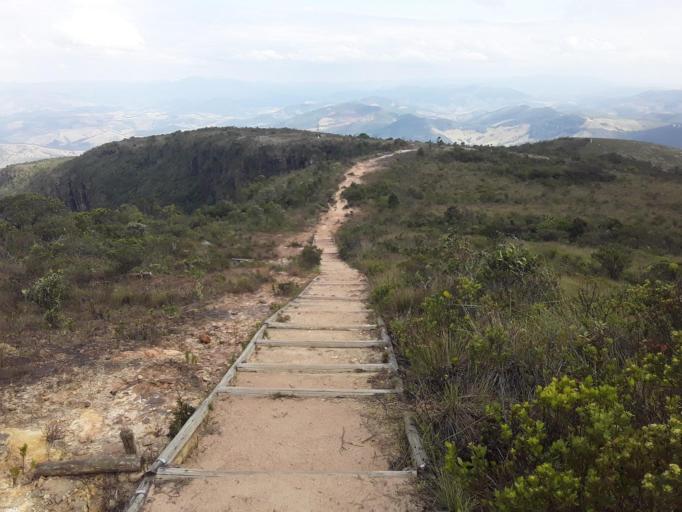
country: BR
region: Minas Gerais
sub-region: Lima Duarte
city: Lima Duarte
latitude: -21.7062
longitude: -43.8715
